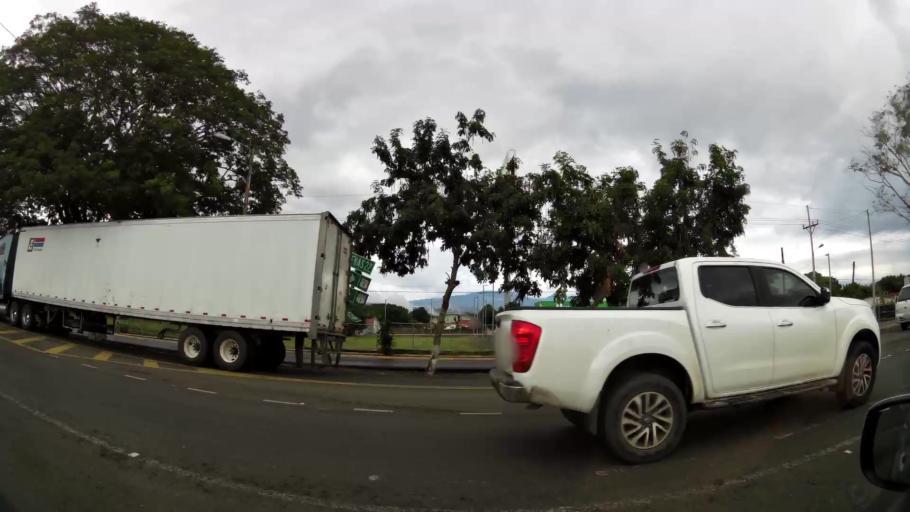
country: CR
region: Puntarenas
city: Esparza
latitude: 9.9953
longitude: -84.6640
